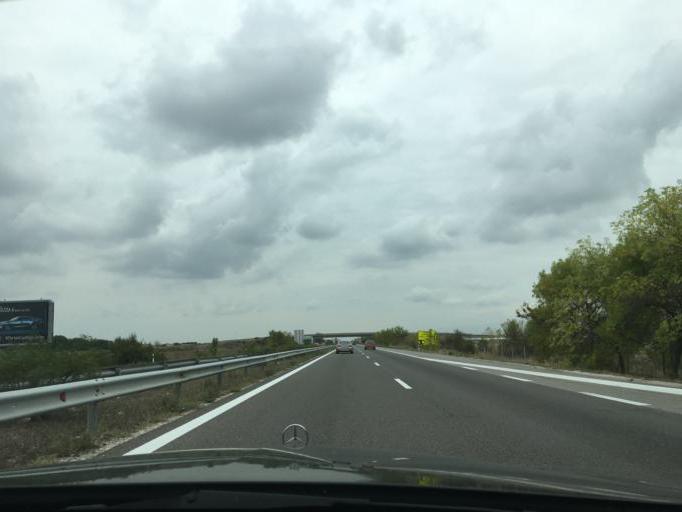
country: BG
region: Pazardzhik
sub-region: Obshtina Pazardzhik
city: Pazardzhik
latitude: 42.2588
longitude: 24.3230
